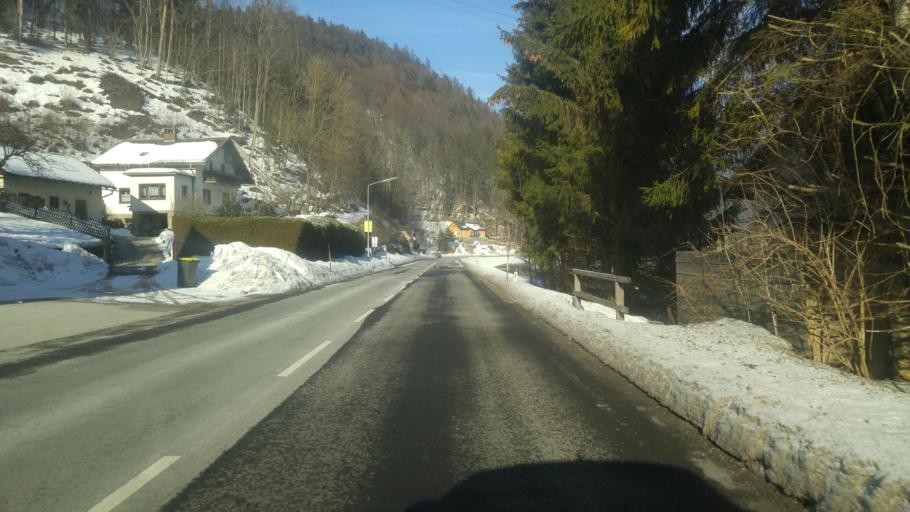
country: AT
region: Lower Austria
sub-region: Politischer Bezirk Lilienfeld
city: Turnitz
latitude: 47.9373
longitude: 15.4973
